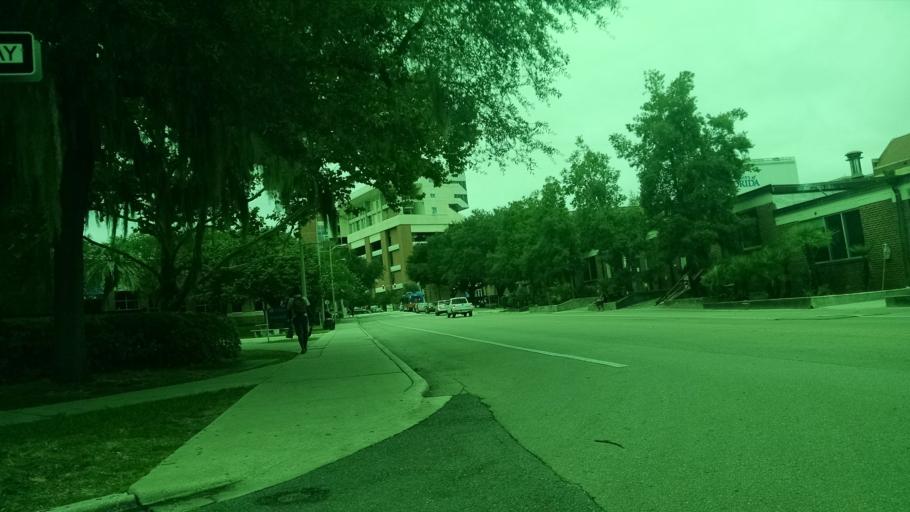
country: US
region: Florida
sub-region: Alachua County
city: Gainesville
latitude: 29.6472
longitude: -82.3498
